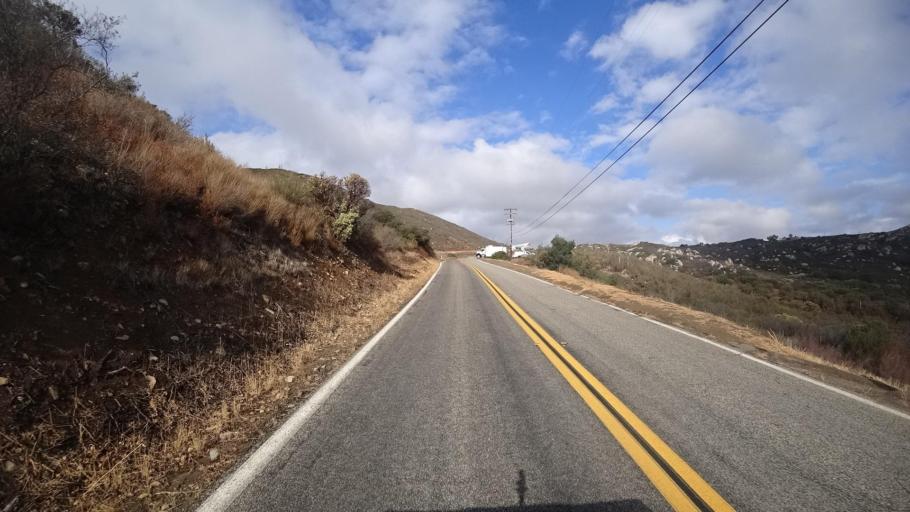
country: MX
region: Baja California
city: Tecate
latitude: 32.6259
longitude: -116.6268
